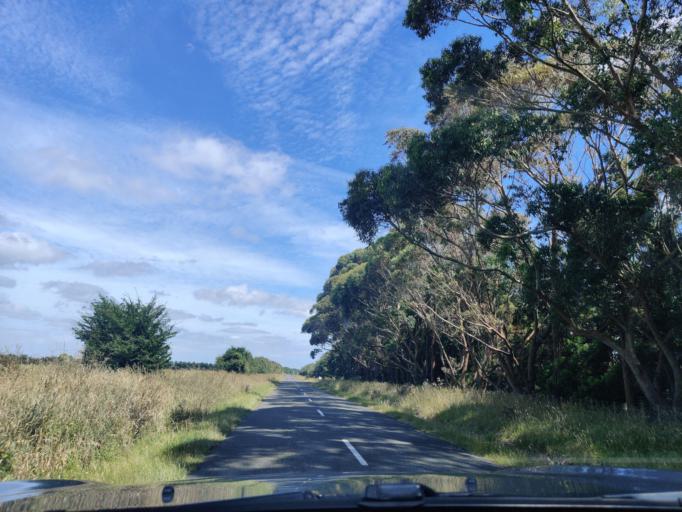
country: NZ
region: Manawatu-Wanganui
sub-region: Rangitikei District
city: Bulls
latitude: -40.1819
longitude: 175.4370
